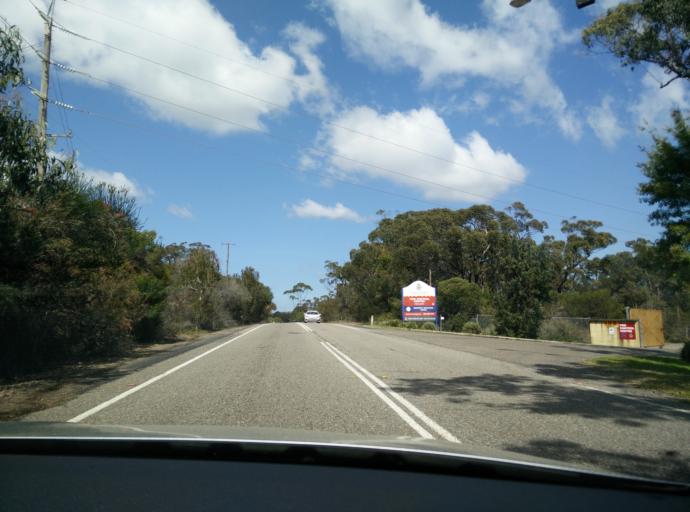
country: AU
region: New South Wales
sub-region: Gosford Shire
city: Point Clare
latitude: -33.4478
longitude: 151.2930
